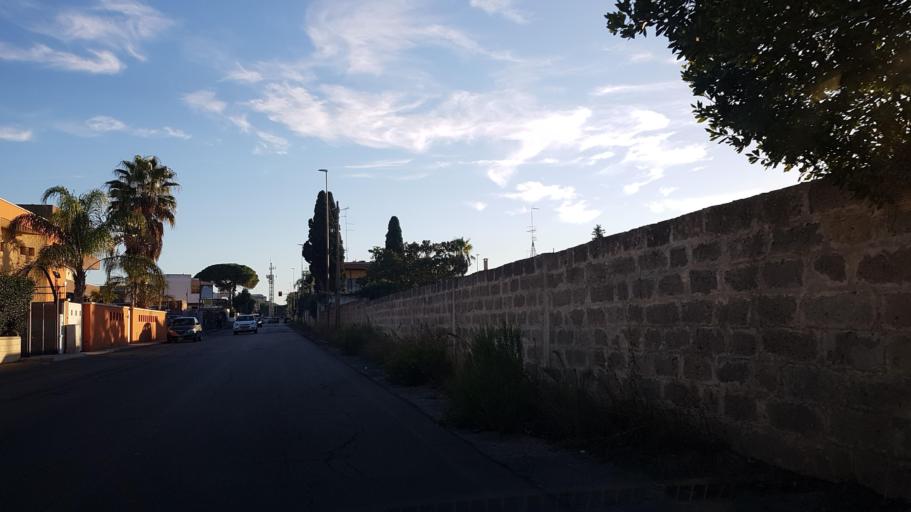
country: IT
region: Apulia
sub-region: Provincia di Lecce
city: Lecce
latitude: 40.3726
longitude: 18.1790
